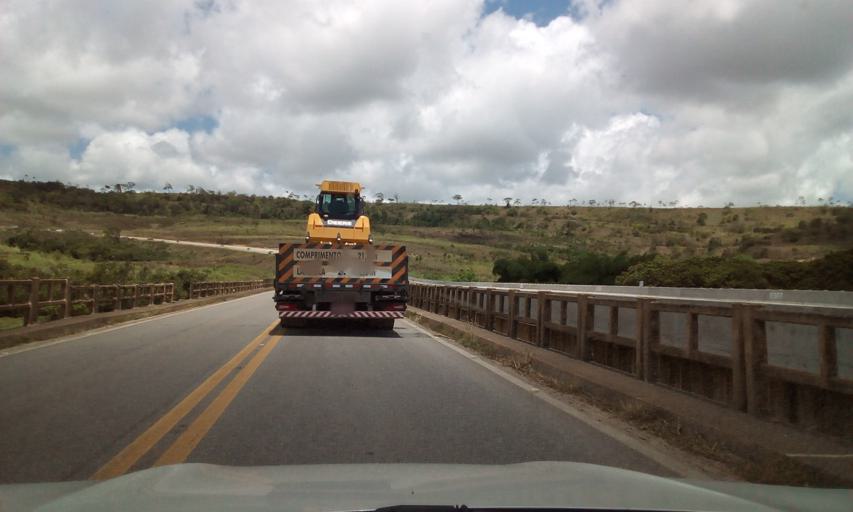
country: BR
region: Alagoas
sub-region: Sao Miguel Dos Campos
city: Sao Miguel dos Campos
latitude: -9.8929
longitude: -36.1369
